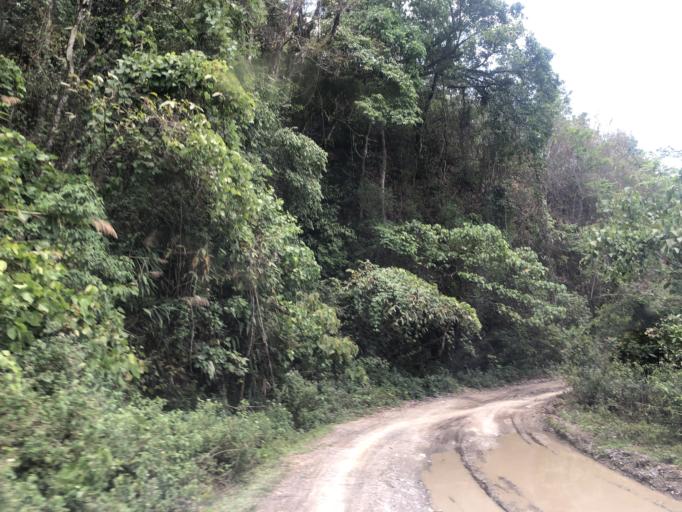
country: LA
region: Phongsali
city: Phongsali
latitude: 21.4460
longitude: 102.1637
